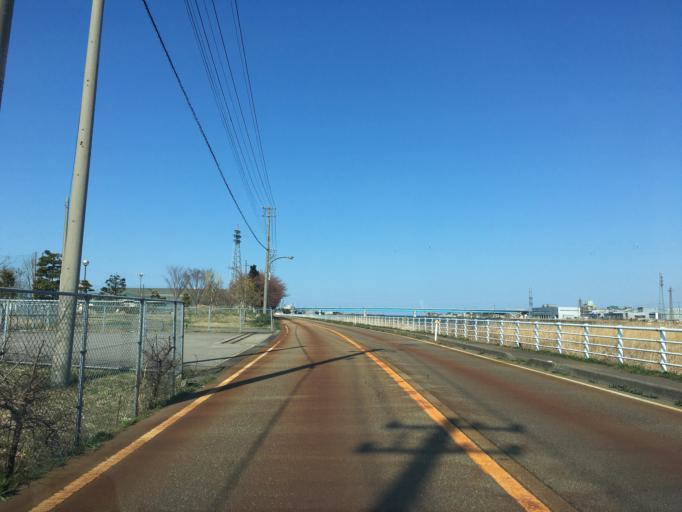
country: JP
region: Toyama
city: Nishishinminato
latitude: 36.7831
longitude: 137.0505
